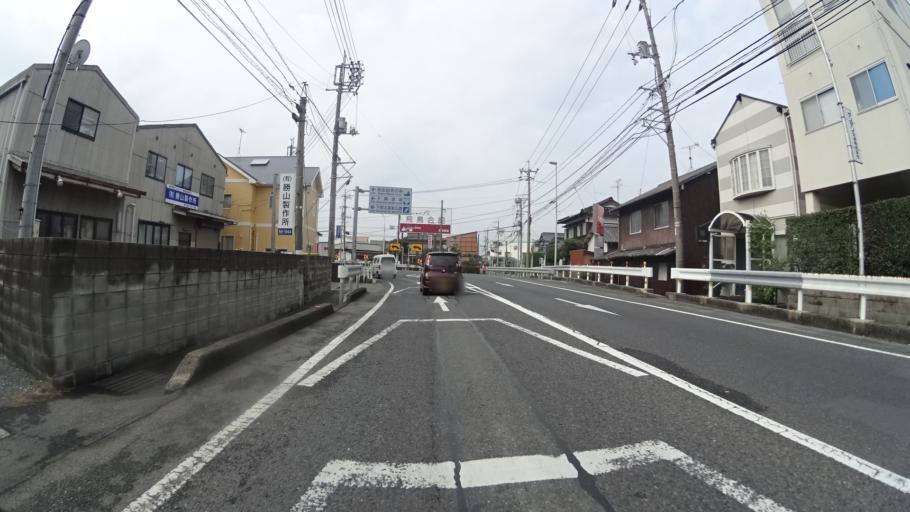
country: JP
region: Yamaguchi
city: Shimonoseki
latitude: 34.0301
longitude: 130.9116
